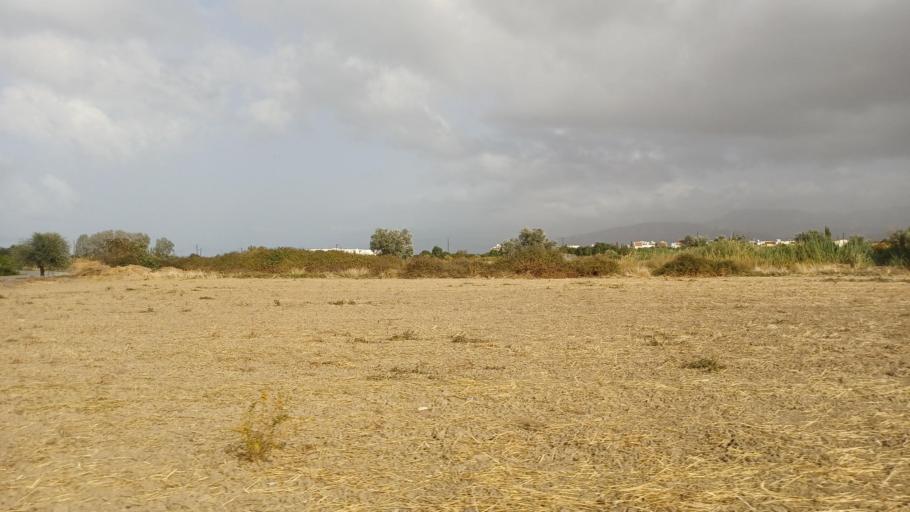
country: CY
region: Pafos
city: Polis
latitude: 35.0409
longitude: 32.4234
